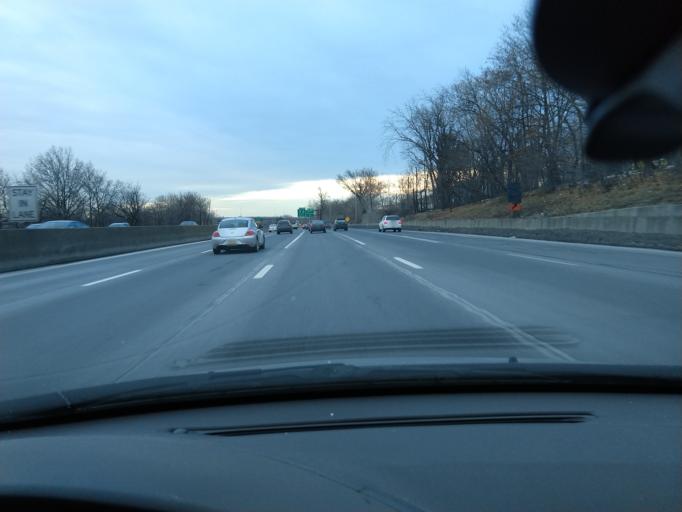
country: US
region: New Jersey
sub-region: Union County
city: Hillside
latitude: 40.7146
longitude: -74.2425
